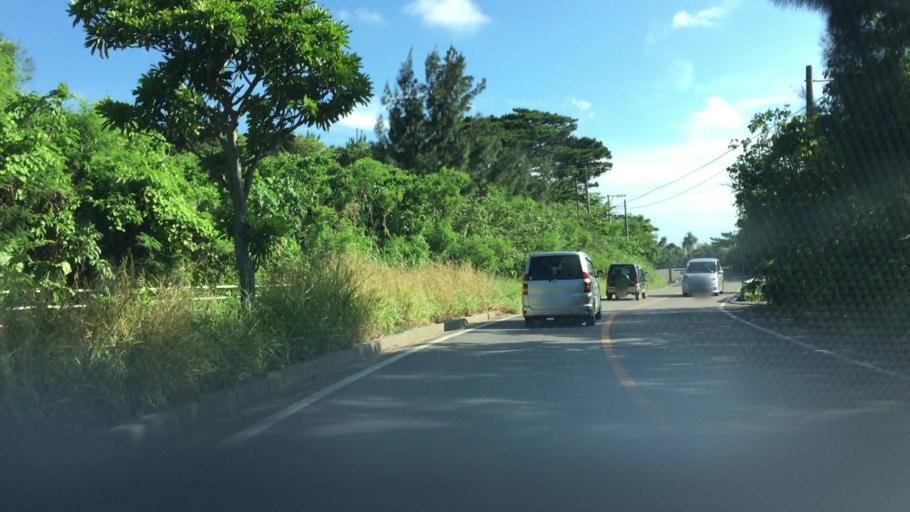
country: JP
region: Okinawa
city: Ishigaki
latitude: 24.4179
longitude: 124.1344
